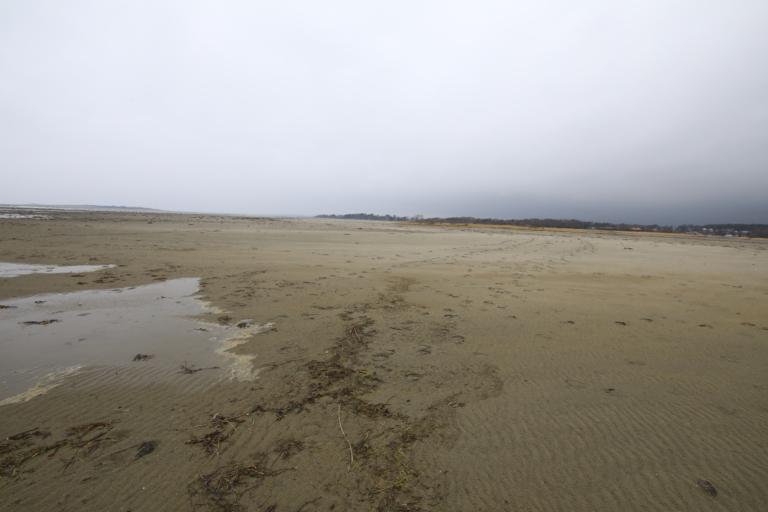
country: SE
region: Halland
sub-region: Kungsbacka Kommun
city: Frillesas
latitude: 57.3048
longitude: 12.1639
